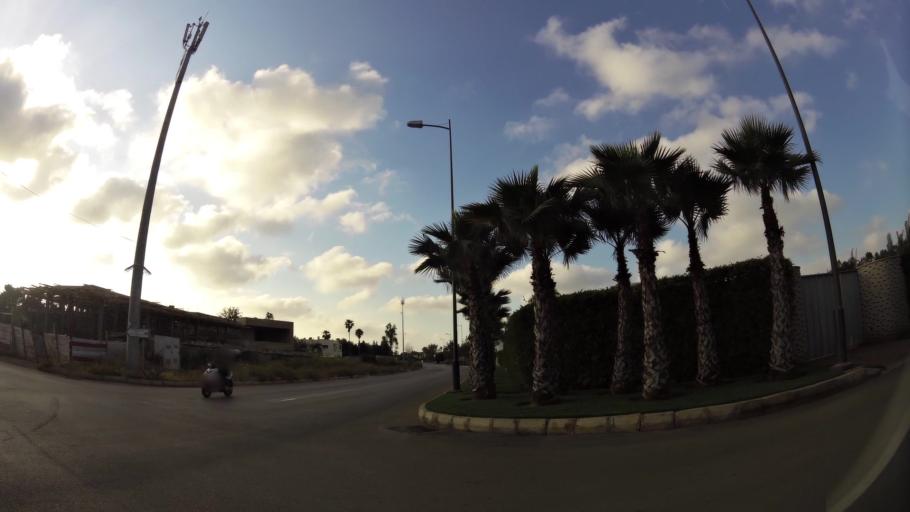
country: MA
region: Rabat-Sale-Zemmour-Zaer
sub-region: Rabat
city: Rabat
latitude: 33.9577
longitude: -6.8416
